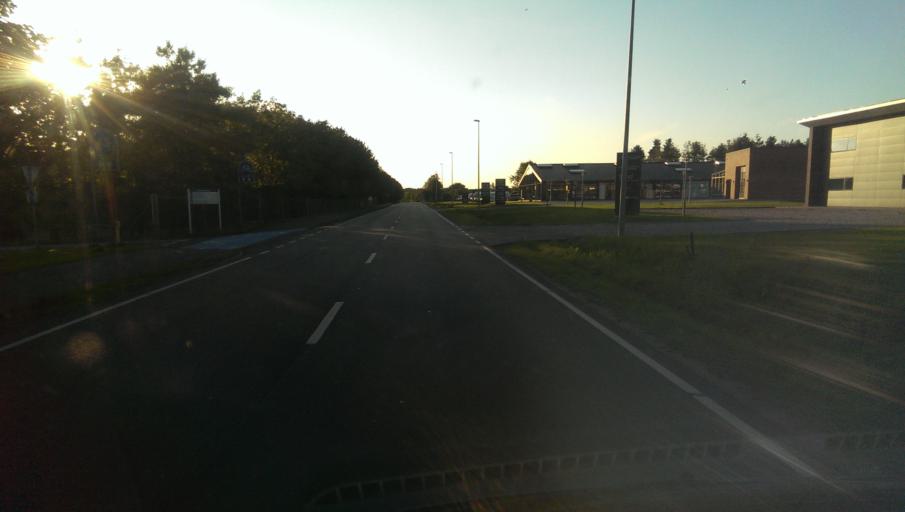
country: DK
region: South Denmark
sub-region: Esbjerg Kommune
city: Esbjerg
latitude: 55.5283
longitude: 8.4538
